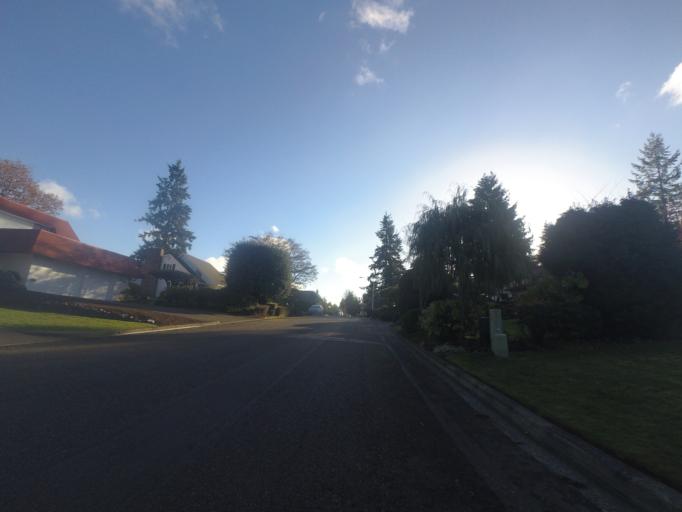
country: US
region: Washington
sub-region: Pierce County
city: Fircrest
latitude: 47.2235
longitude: -122.5256
